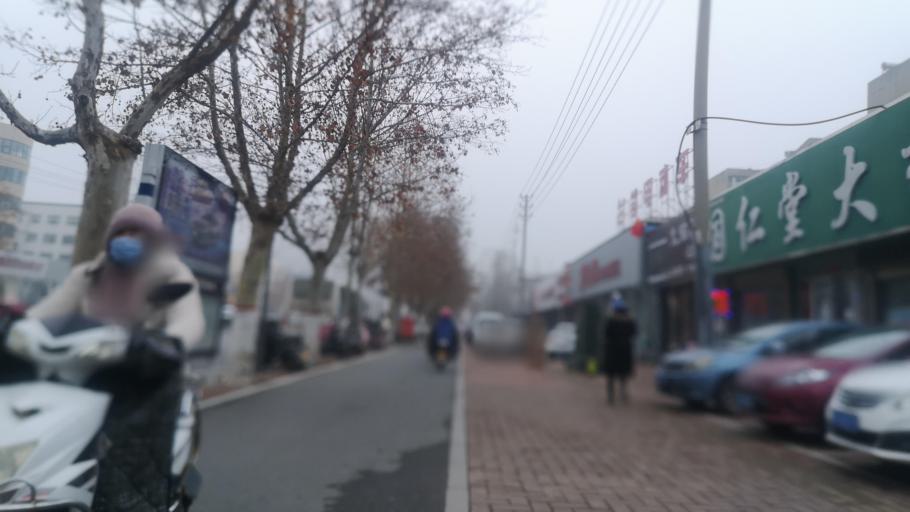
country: CN
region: Henan Sheng
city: Zhongyuanlu
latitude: 35.7638
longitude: 115.0682
